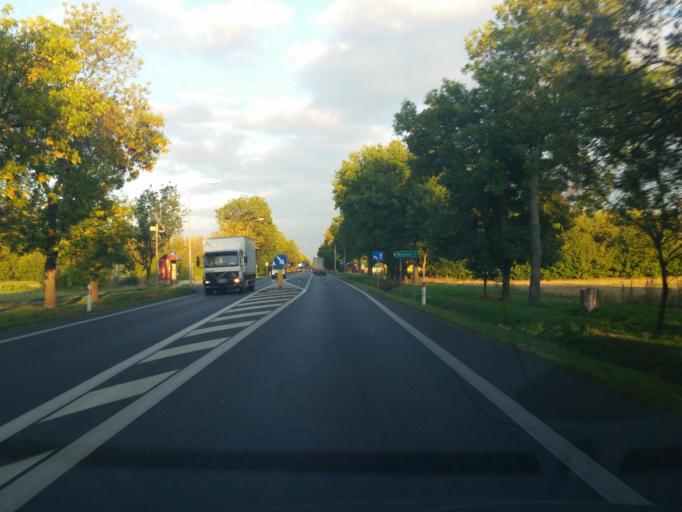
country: PL
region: Masovian Voivodeship
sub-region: Powiat warszawski zachodni
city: Jozefow
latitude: 52.2124
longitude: 20.7130
